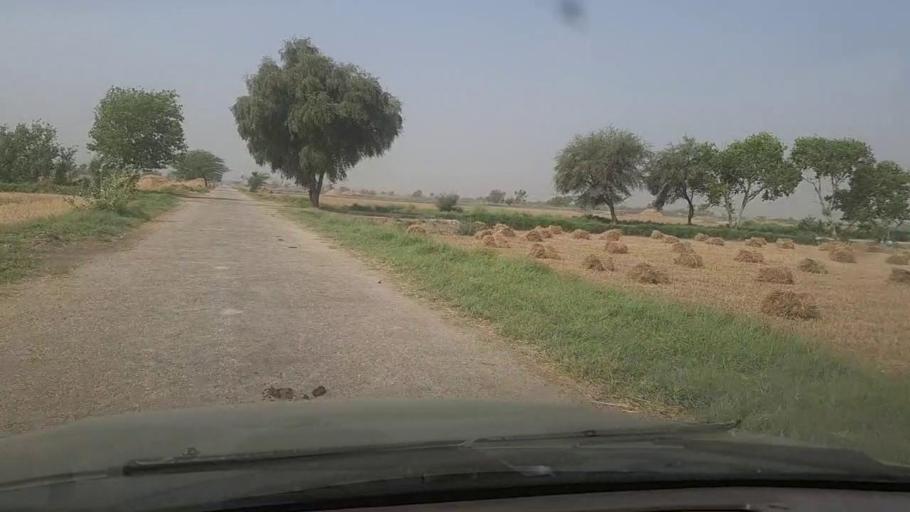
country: PK
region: Sindh
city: Garhi Yasin
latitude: 27.8855
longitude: 68.5741
